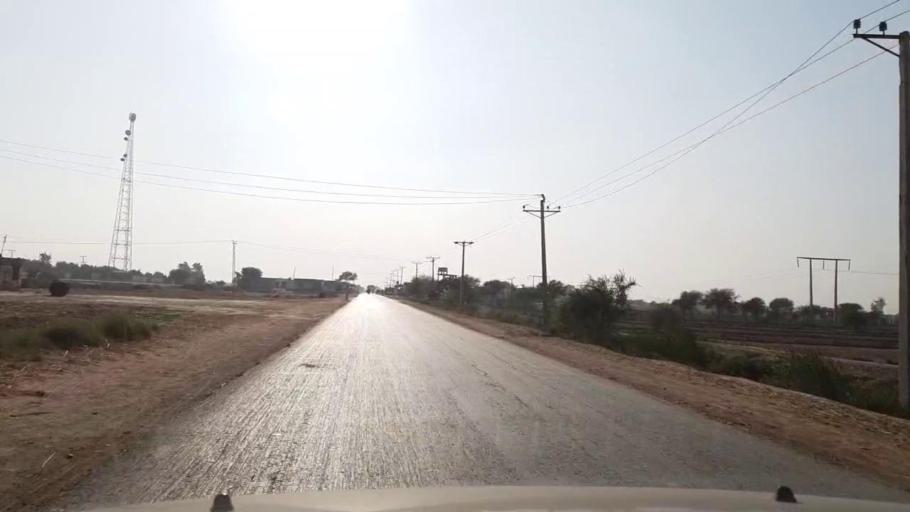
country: PK
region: Sindh
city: Bulri
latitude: 24.9960
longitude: 68.3852
